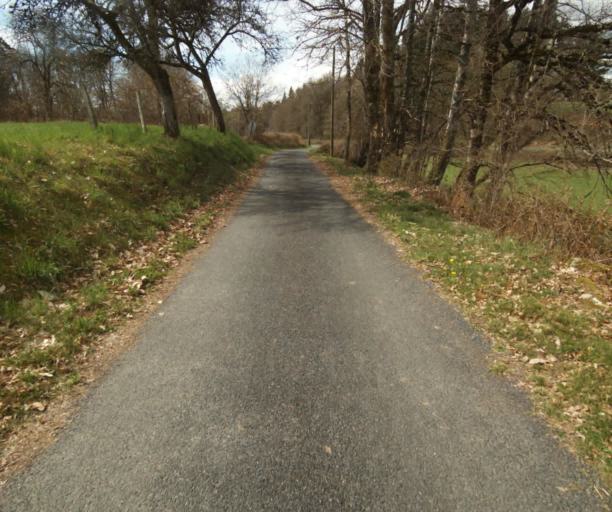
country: FR
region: Limousin
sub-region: Departement de la Correze
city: Correze
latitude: 45.3779
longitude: 1.9002
